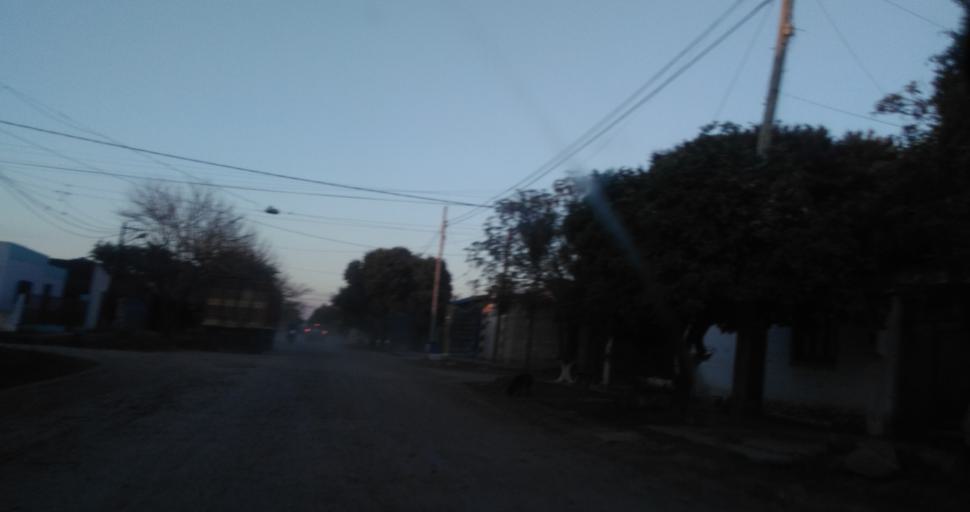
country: AR
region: Chaco
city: Fontana
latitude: -27.4291
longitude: -58.9987
